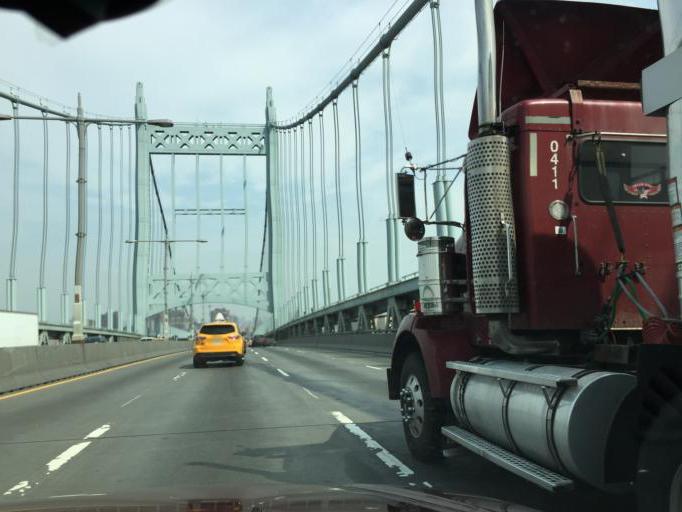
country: US
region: New York
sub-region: New York County
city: Manhattan
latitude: 40.7802
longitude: -73.9270
